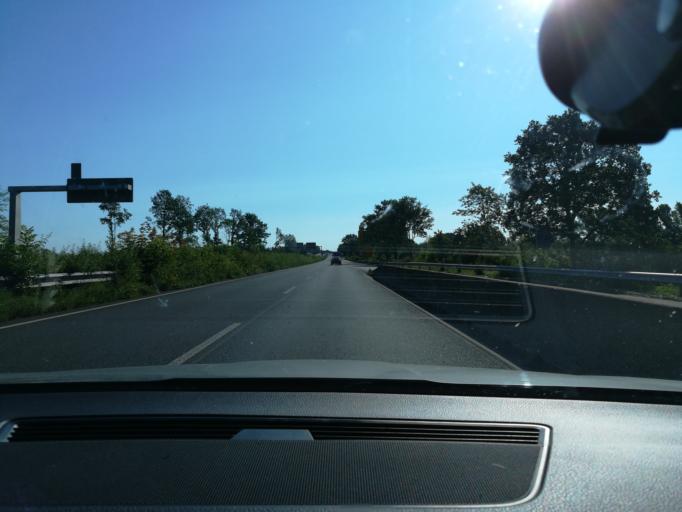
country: DE
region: North Rhine-Westphalia
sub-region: Regierungsbezirk Detmold
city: Minden
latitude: 52.2675
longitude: 8.9162
